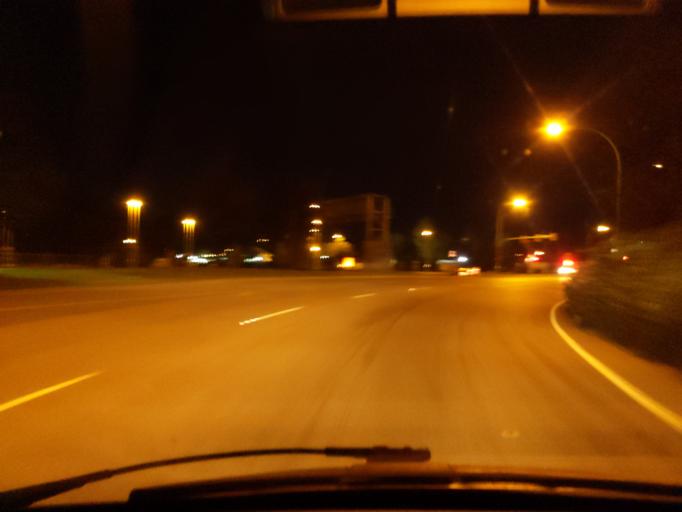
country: CA
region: British Columbia
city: New Westminster
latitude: 49.2039
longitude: -122.8776
